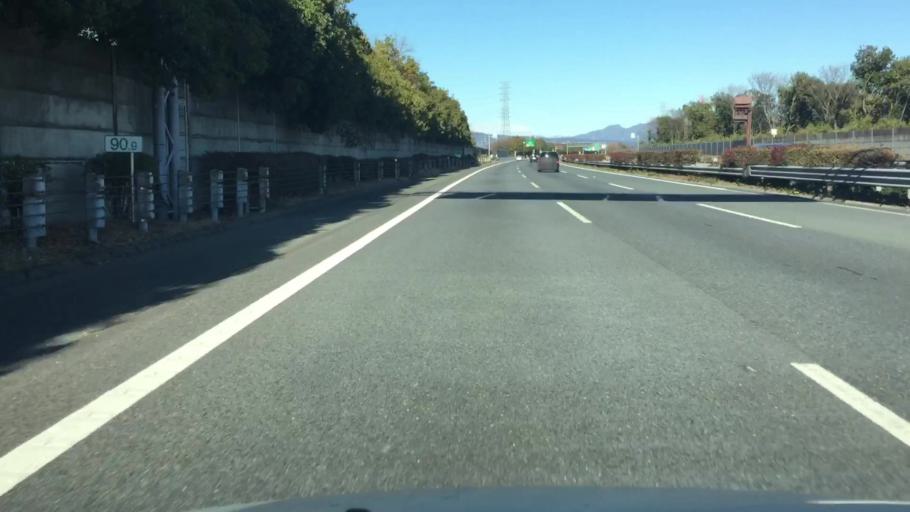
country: JP
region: Gunma
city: Takasaki
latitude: 36.3640
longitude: 139.0326
